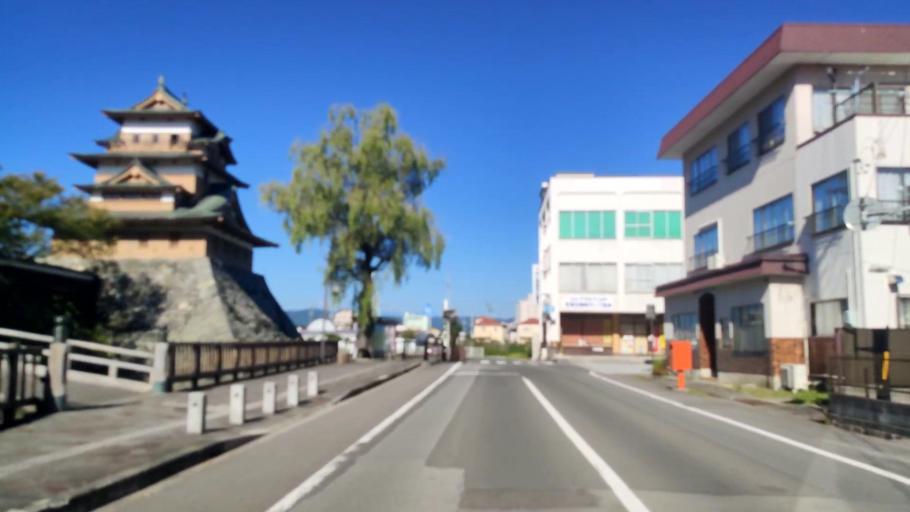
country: JP
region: Nagano
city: Suwa
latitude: 36.0398
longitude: 138.1129
